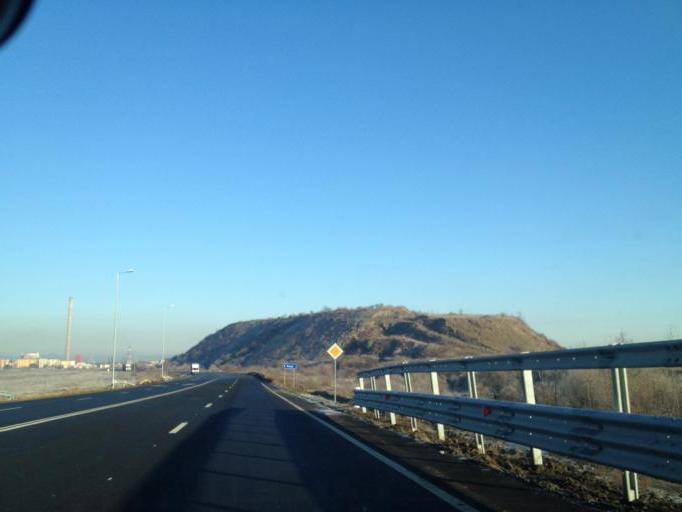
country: RO
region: Brasov
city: Brasov
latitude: 45.6380
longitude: 25.6568
